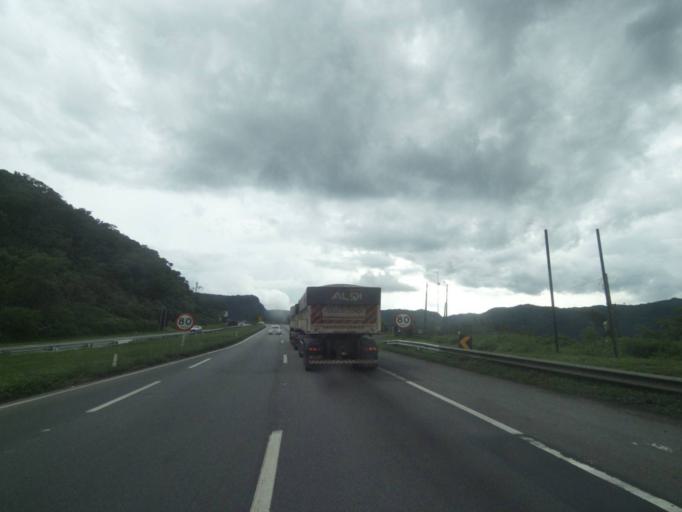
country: BR
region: Parana
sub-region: Antonina
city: Antonina
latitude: -25.5798
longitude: -48.8724
